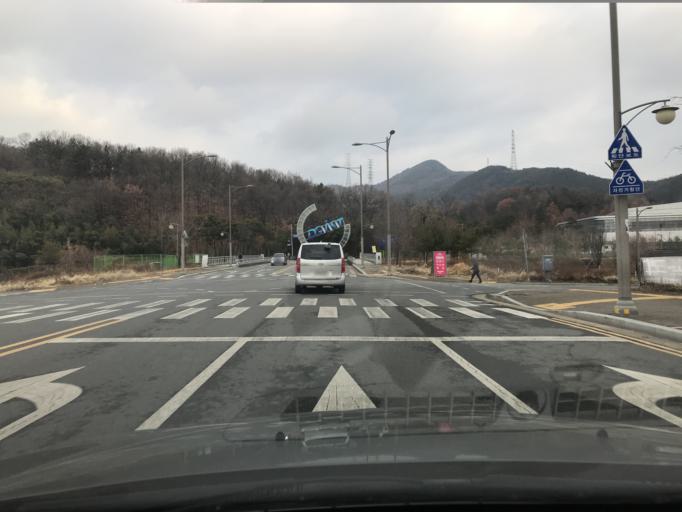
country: KR
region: Daegu
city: Hwawon
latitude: 35.6989
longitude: 128.4578
